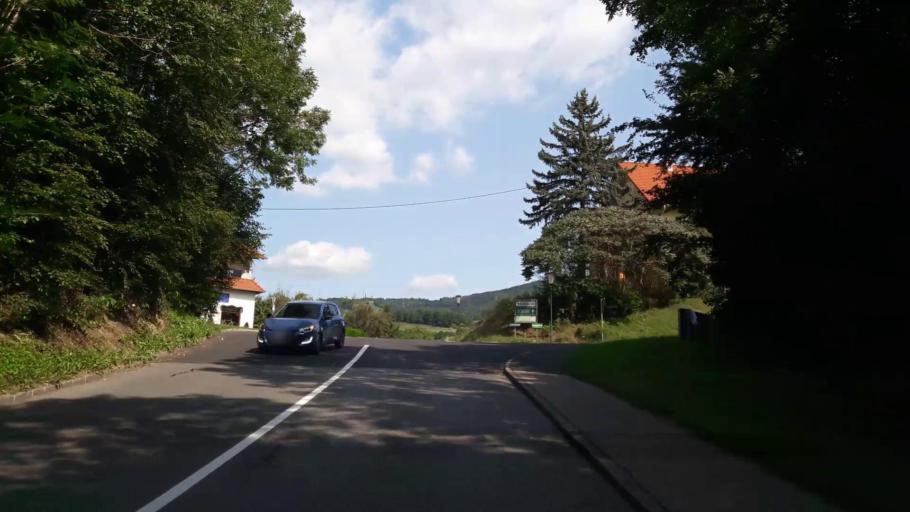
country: AT
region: Styria
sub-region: Politischer Bezirk Hartberg-Fuerstenfeld
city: Stubenberg
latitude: 47.2440
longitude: 15.7971
